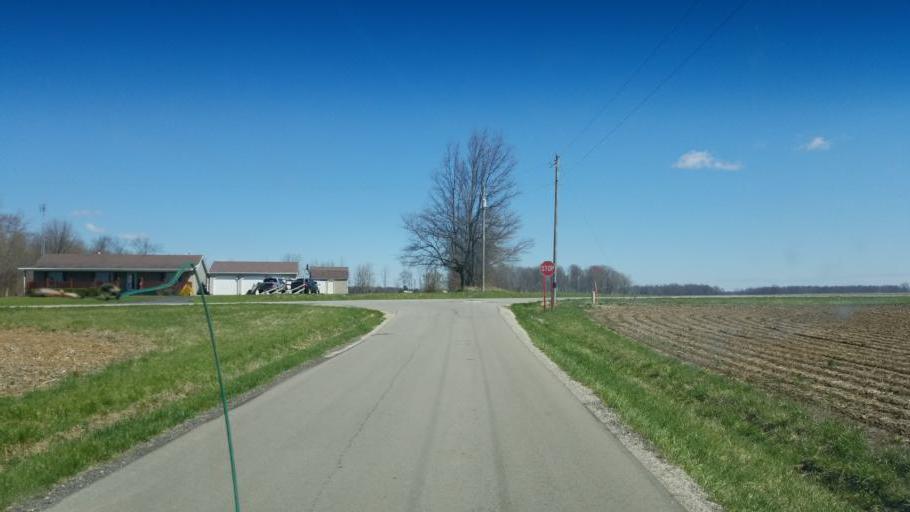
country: US
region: Ohio
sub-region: Crawford County
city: Crestline
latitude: 40.8923
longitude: -82.8359
